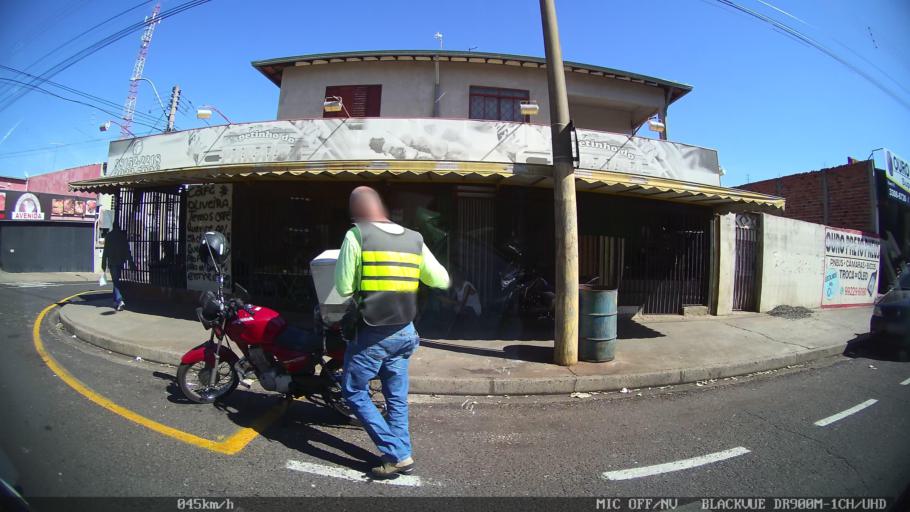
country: BR
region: Sao Paulo
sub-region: Sao Jose Do Rio Preto
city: Sao Jose do Rio Preto
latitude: -20.7540
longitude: -49.4059
